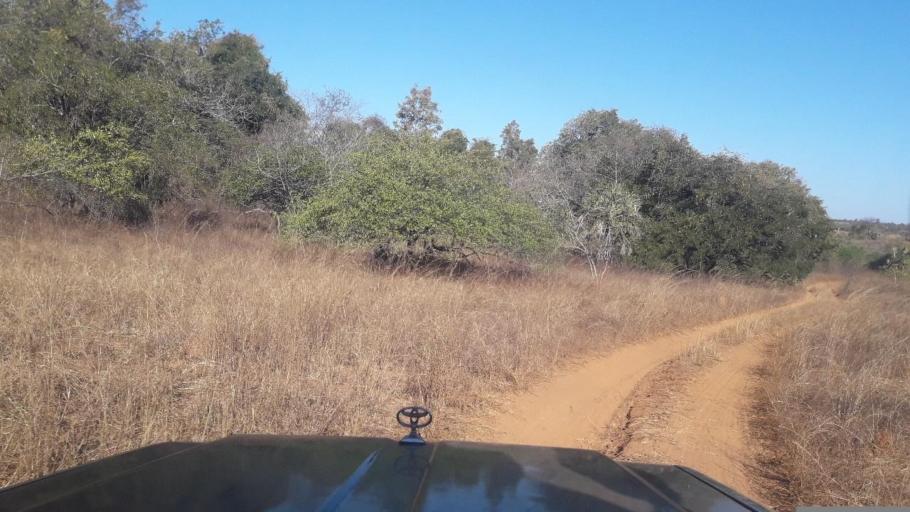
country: MG
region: Boeny
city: Sitampiky
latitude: -16.4158
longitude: 45.6093
